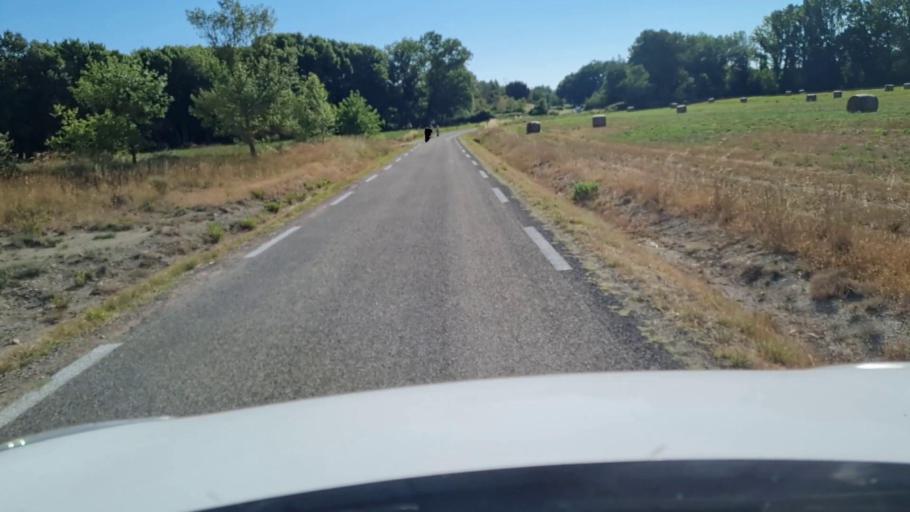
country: FR
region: Languedoc-Roussillon
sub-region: Departement du Gard
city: Sommieres
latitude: 43.8326
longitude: 4.0511
